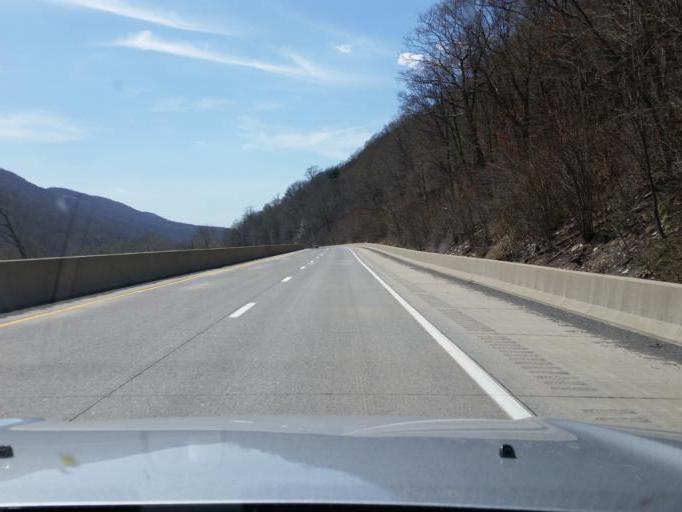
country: US
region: Pennsylvania
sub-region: Mifflin County
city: Lewistown
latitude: 40.5911
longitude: -77.5142
